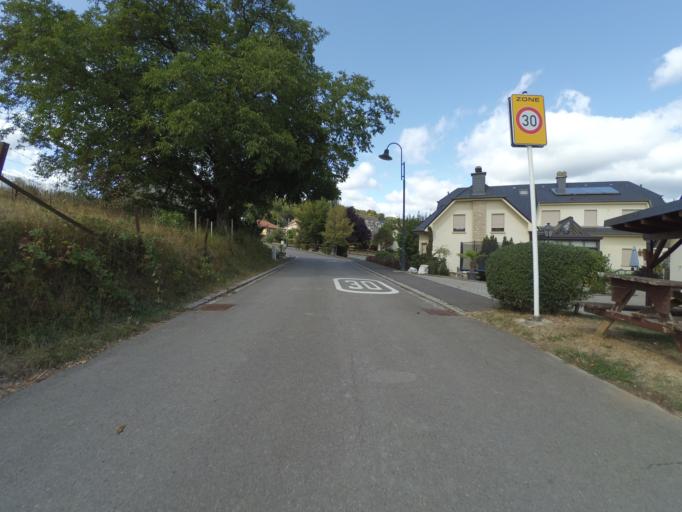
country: LU
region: Grevenmacher
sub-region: Canton de Remich
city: Lenningen
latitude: 49.6184
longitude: 6.3560
